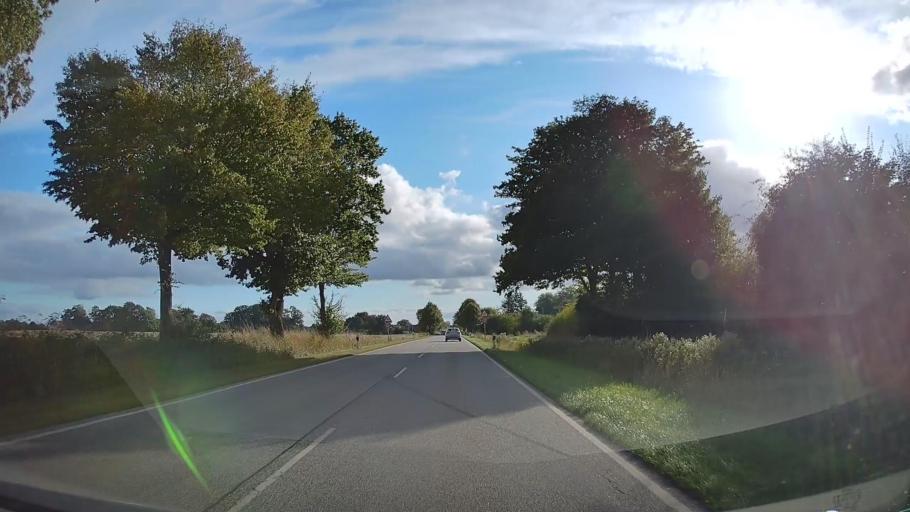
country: DE
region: Schleswig-Holstein
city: Rabel
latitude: 54.7167
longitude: 9.9525
